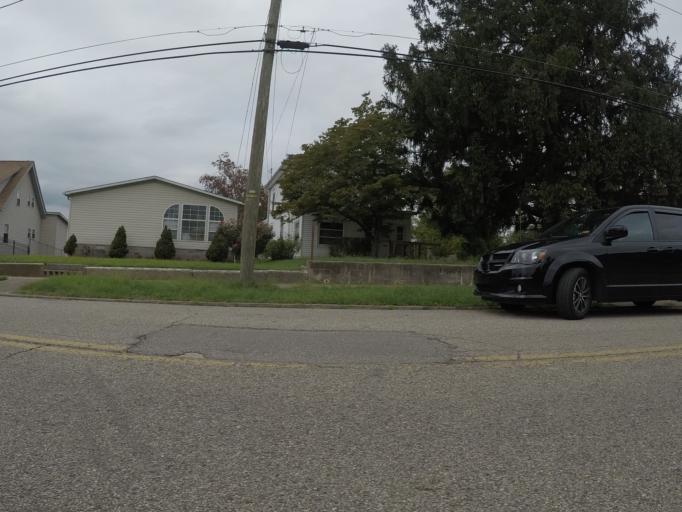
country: US
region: West Virginia
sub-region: Cabell County
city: Huntington
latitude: 38.4272
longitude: -82.3838
